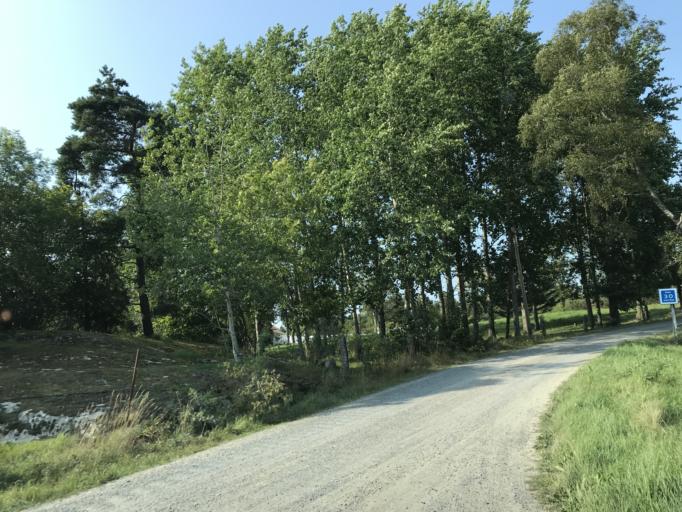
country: SE
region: Stockholm
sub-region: Norrtalje Kommun
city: Bjorko
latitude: 59.8469
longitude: 19.0144
